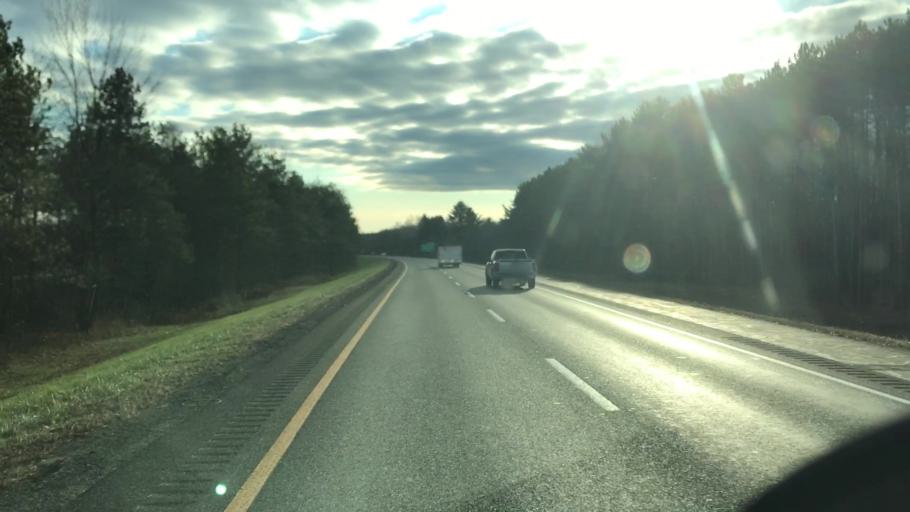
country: US
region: Maine
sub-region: Kennebec County
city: Oakland
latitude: 44.5243
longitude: -69.6969
